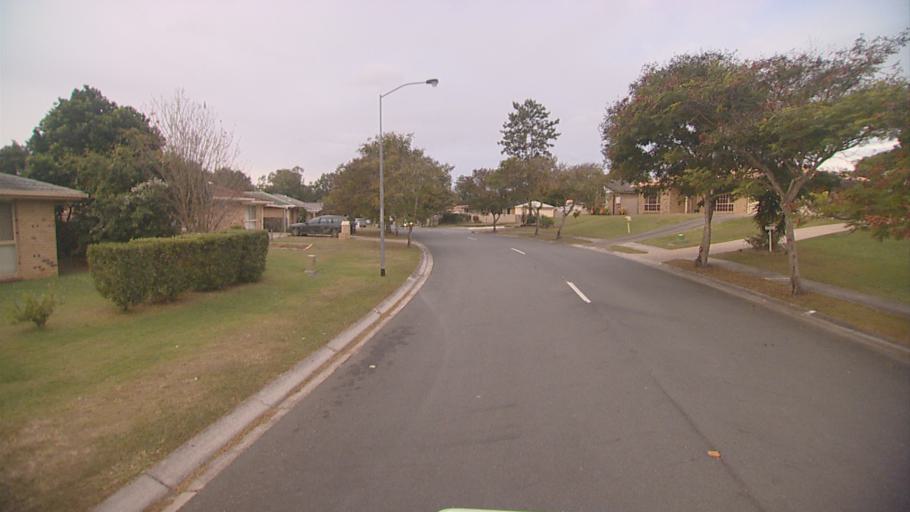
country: AU
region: Queensland
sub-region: Logan
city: Park Ridge South
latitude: -27.6747
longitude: 153.0225
